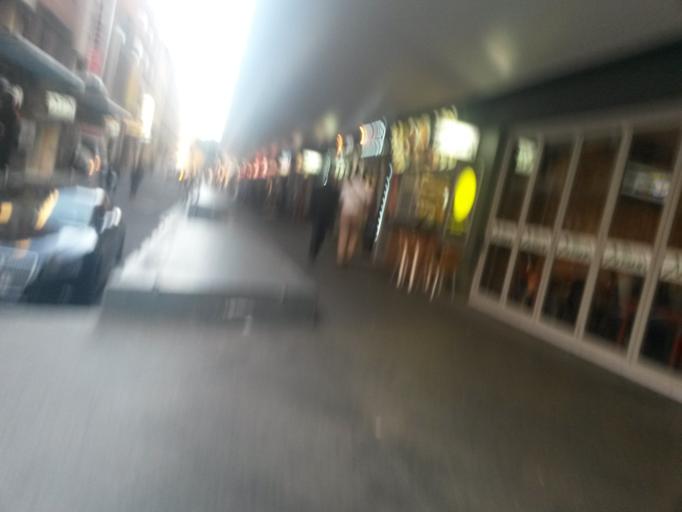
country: AU
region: New South Wales
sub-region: City of Sydney
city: Haymarket
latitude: -33.8763
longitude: 151.2039
